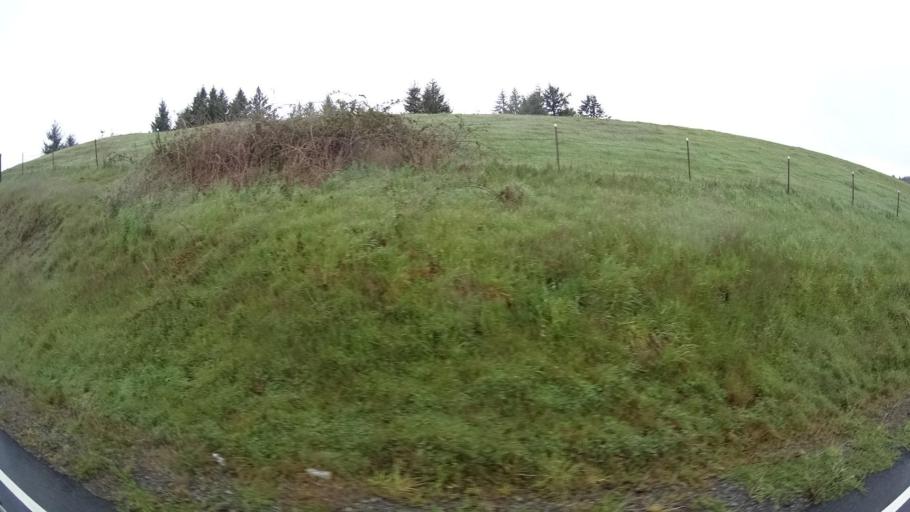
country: US
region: California
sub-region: Humboldt County
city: Westhaven-Moonstone
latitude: 41.1658
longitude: -123.9134
